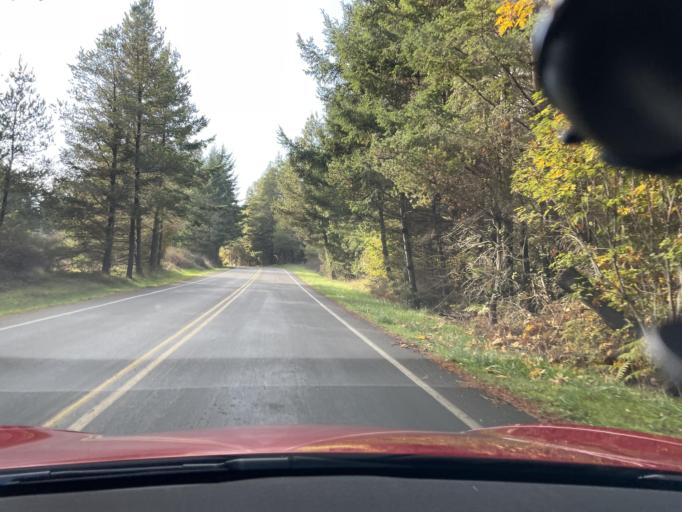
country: US
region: Washington
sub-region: San Juan County
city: Friday Harbor
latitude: 48.4691
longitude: -123.0198
